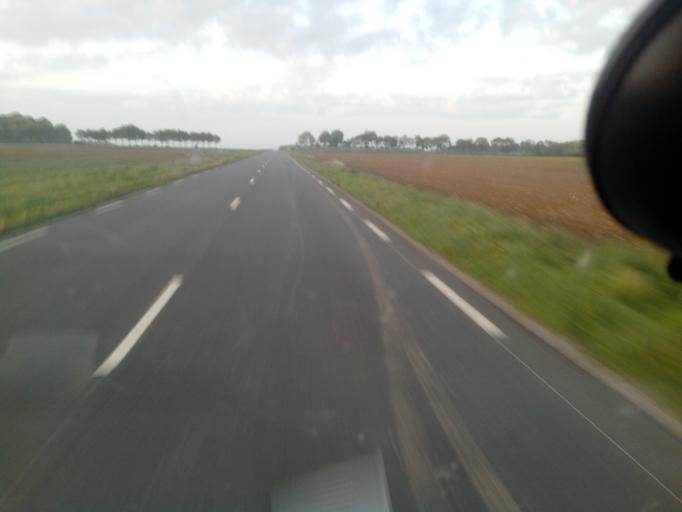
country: FR
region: Picardie
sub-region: Departement de la Somme
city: Crecy-en-Ponthieu
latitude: 50.2036
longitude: 1.8971
